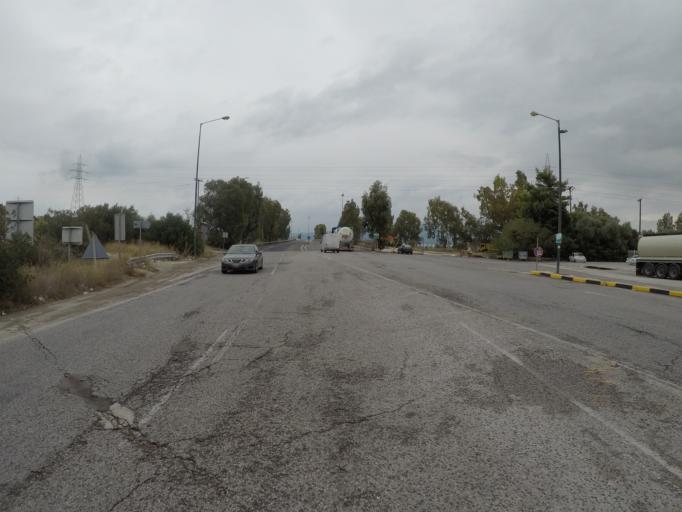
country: GR
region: Peloponnese
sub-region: Nomos Korinthias
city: Isthmia
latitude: 37.9273
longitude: 22.9973
